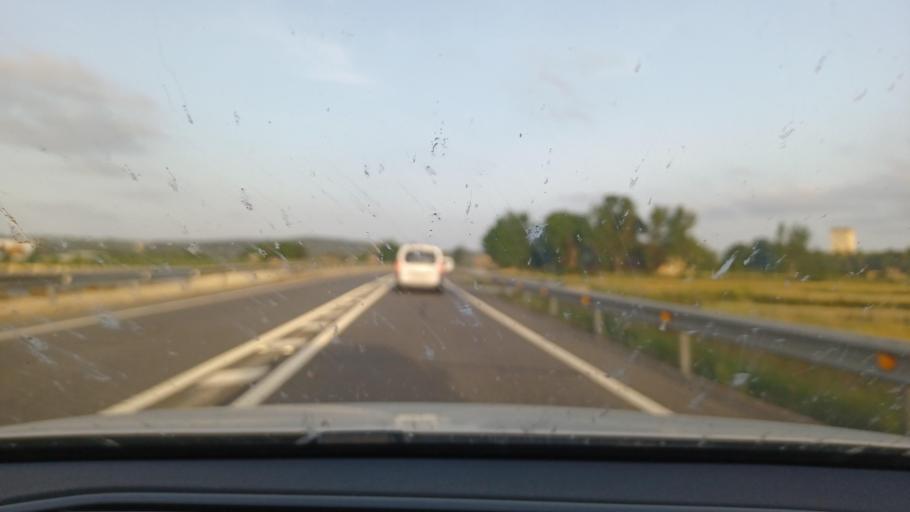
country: ES
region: Catalonia
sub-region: Provincia de Tarragona
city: Amposta
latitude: 40.7473
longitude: 0.5576
